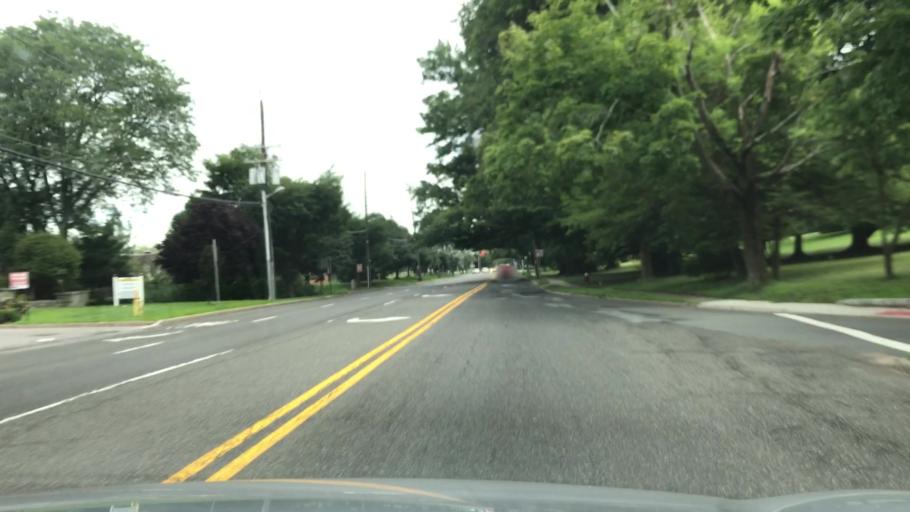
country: US
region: New Jersey
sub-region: Bergen County
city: Oradell
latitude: 40.9626
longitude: -74.0307
